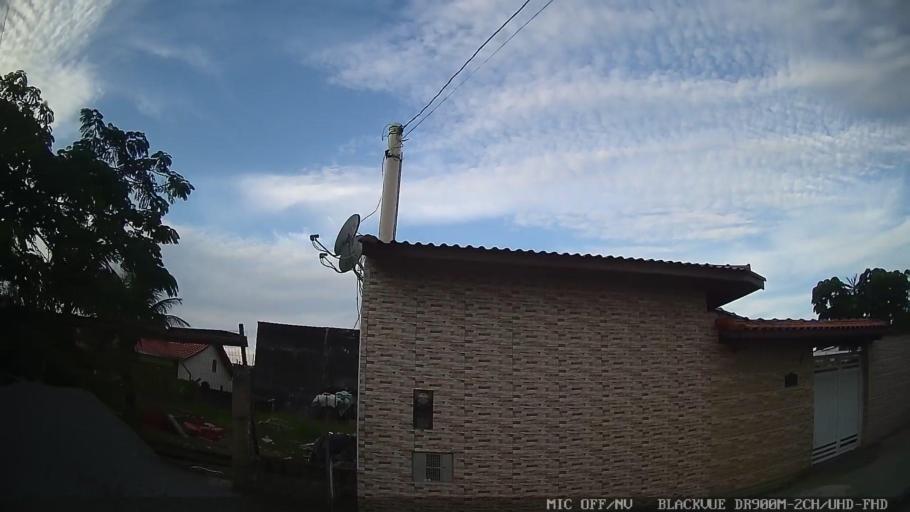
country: BR
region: Sao Paulo
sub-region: Itanhaem
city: Itanhaem
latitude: -24.1660
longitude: -46.7785
